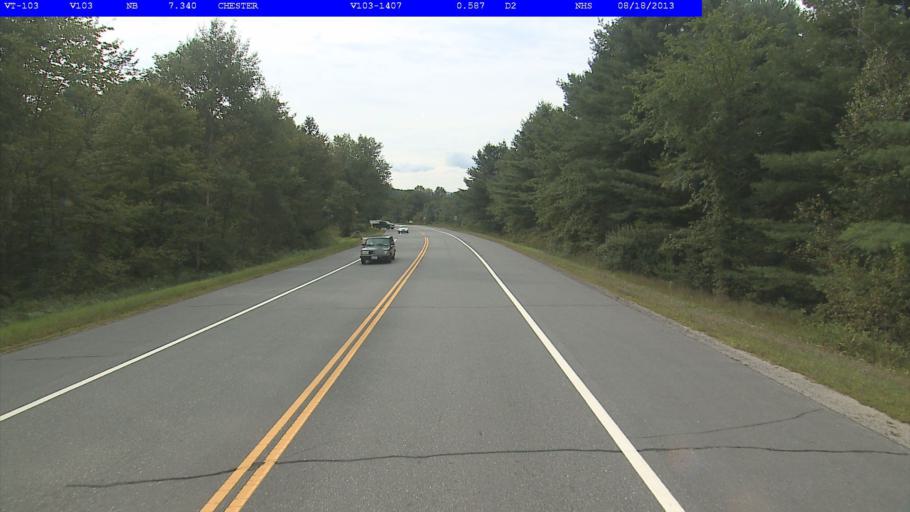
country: US
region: Vermont
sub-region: Windsor County
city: Chester
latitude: 43.2406
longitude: -72.5620
